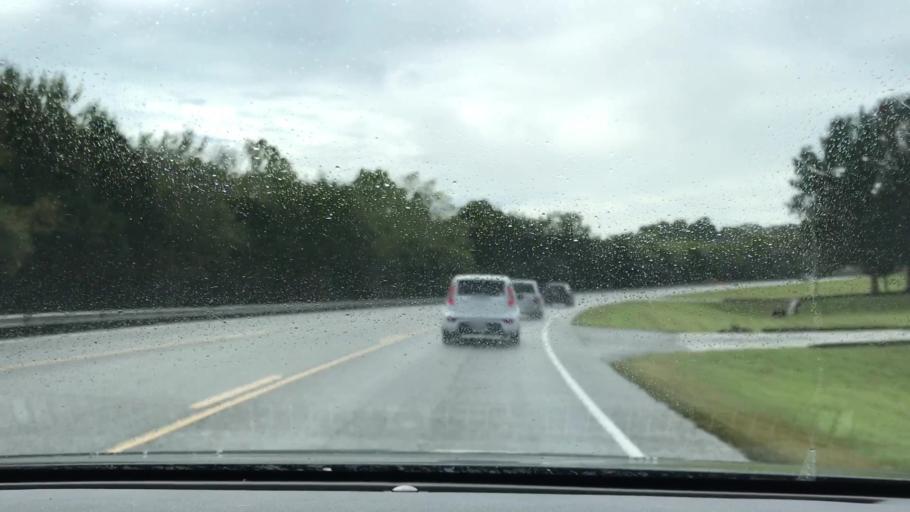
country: US
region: Tennessee
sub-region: Smith County
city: South Carthage
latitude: 36.2210
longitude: -85.9486
